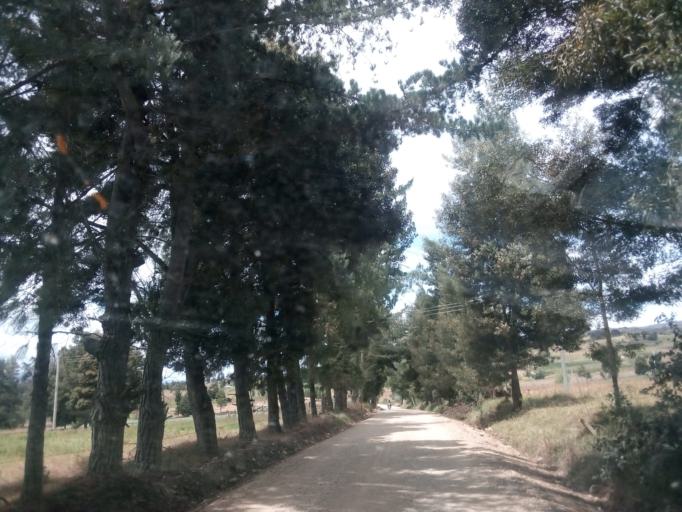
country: CO
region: Boyaca
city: Toca
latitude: 5.5925
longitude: -73.1631
